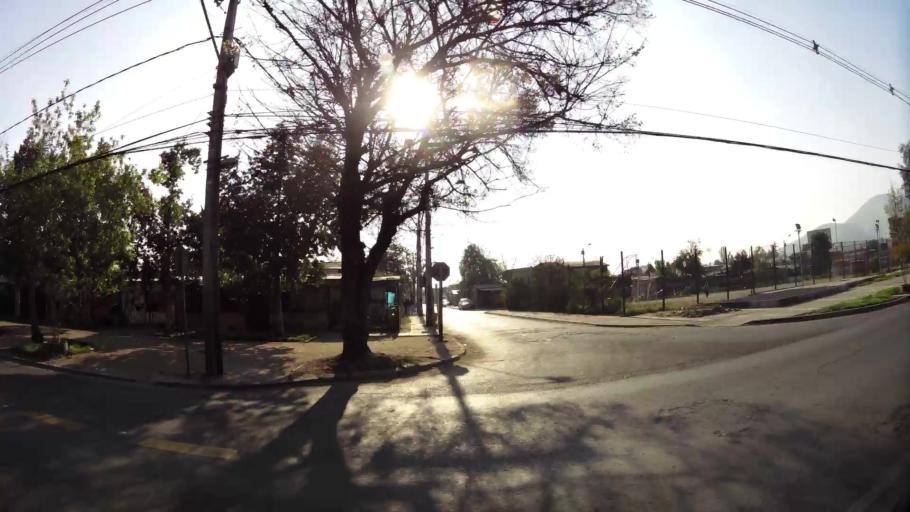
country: CL
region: Santiago Metropolitan
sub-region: Provincia de Santiago
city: Santiago
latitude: -33.3847
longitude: -70.6411
